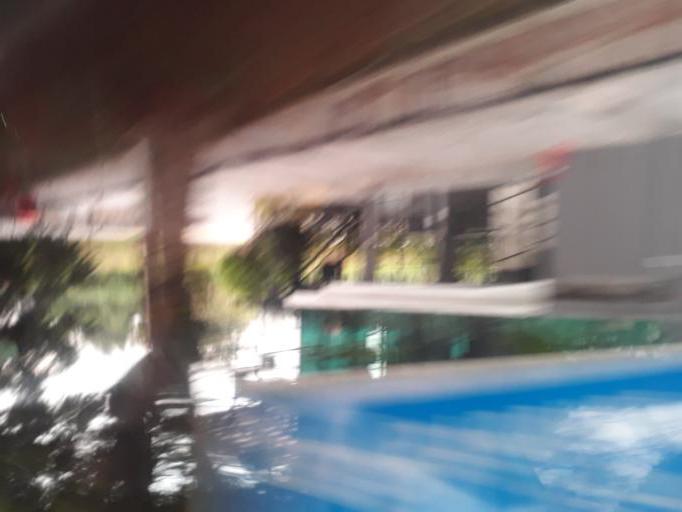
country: MY
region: Perak
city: Ipoh
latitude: 4.6011
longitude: 101.1153
